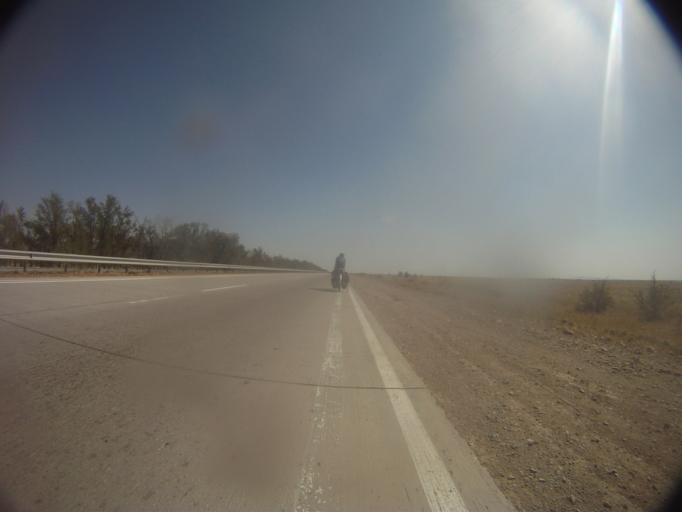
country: KZ
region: Zhambyl
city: Taraz
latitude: 42.7865
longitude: 71.0551
